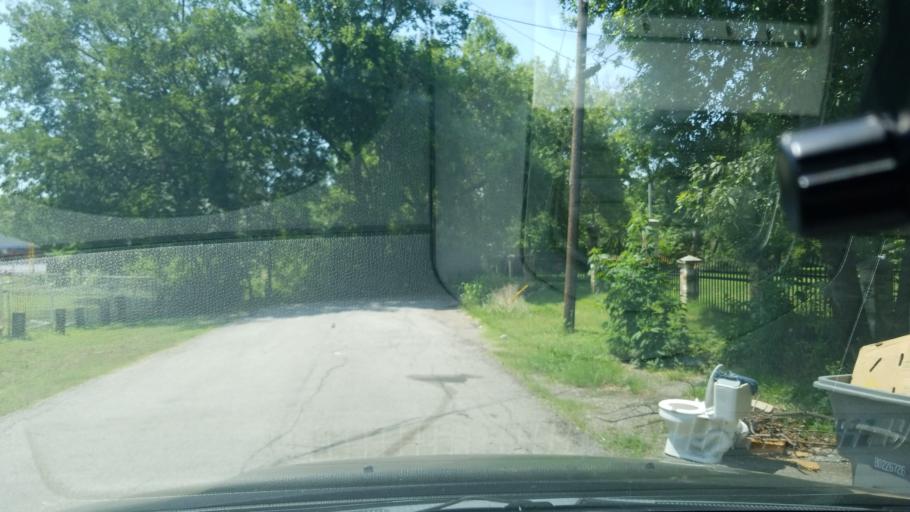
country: US
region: Texas
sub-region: Dallas County
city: Balch Springs
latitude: 32.7325
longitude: -96.6927
